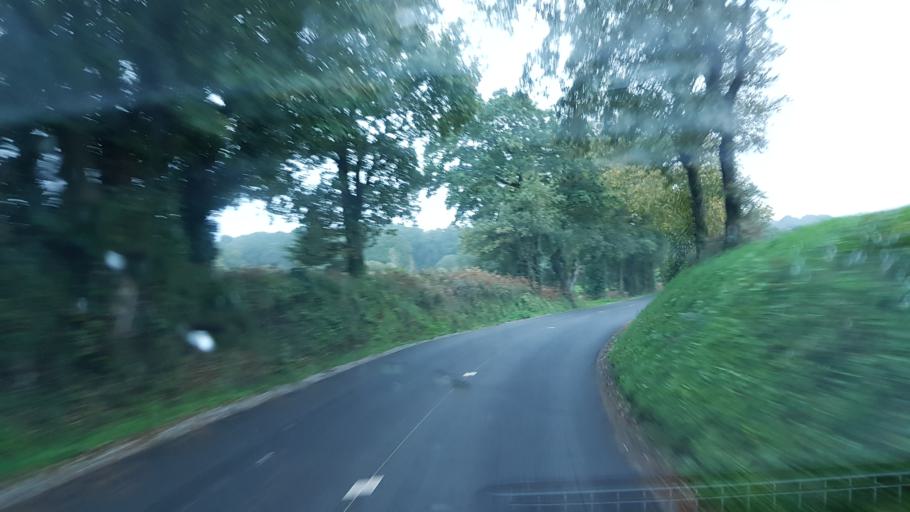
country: FR
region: Brittany
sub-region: Departement du Morbihan
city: Trefflean
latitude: 47.6552
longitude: -2.6280
